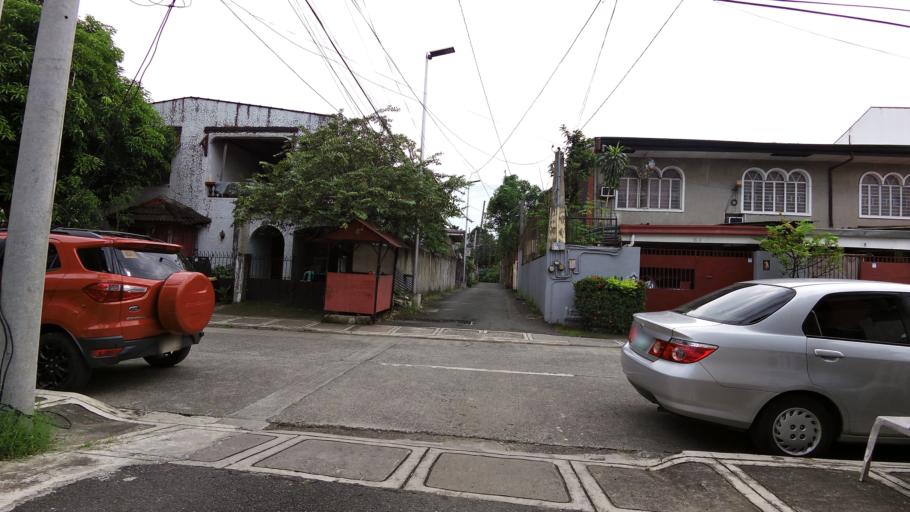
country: PH
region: Metro Manila
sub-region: Quezon City
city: Quezon City
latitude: 14.6373
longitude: 121.0574
